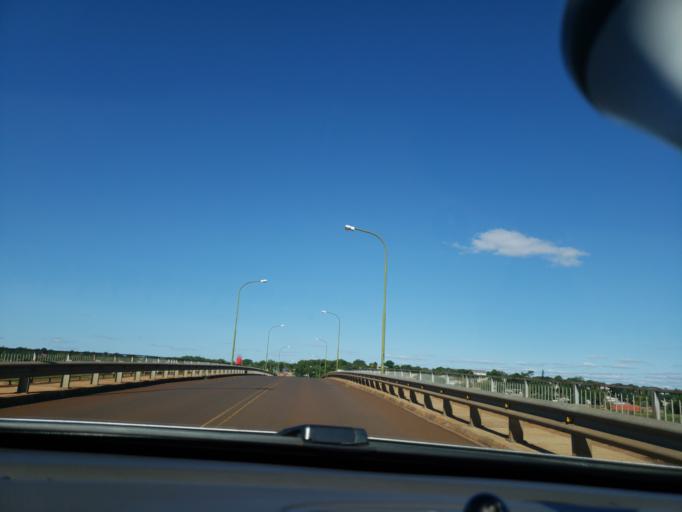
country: AR
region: Misiones
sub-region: Departamento de Capital
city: Posadas
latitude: -27.3823
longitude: -55.9560
